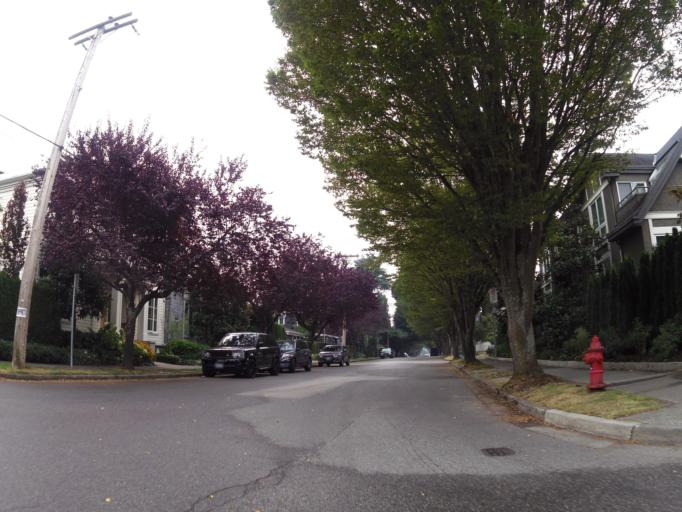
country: CA
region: British Columbia
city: West End
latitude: 49.2762
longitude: -123.1477
